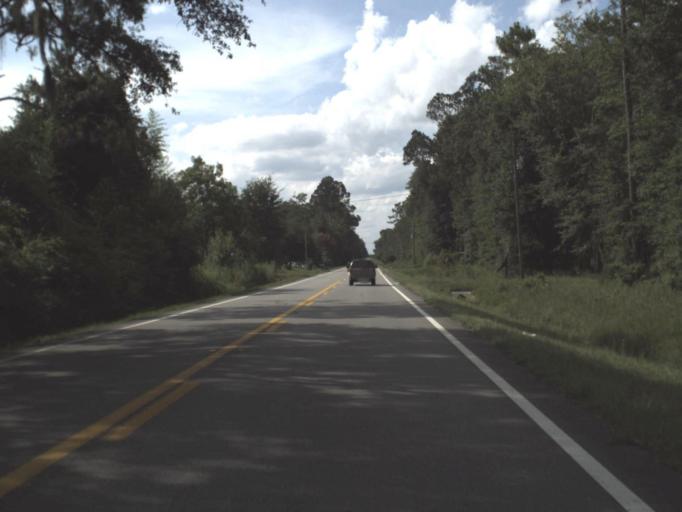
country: US
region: Florida
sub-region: Taylor County
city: Perry
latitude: 30.3455
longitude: -83.6484
